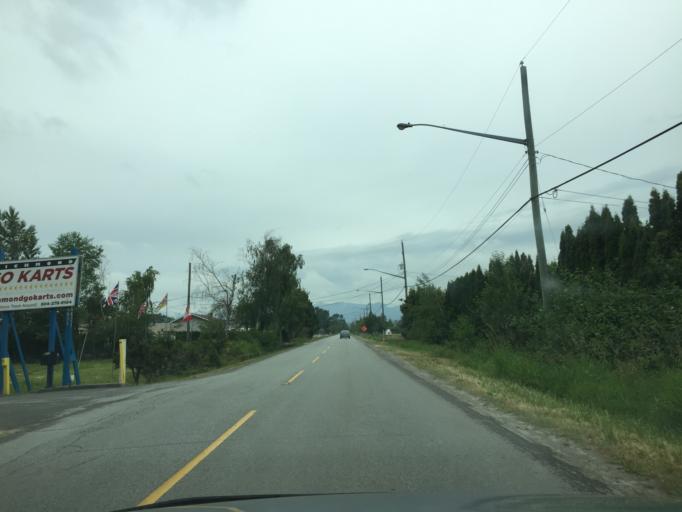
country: CA
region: British Columbia
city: Richmond
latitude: 49.1647
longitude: -123.0805
